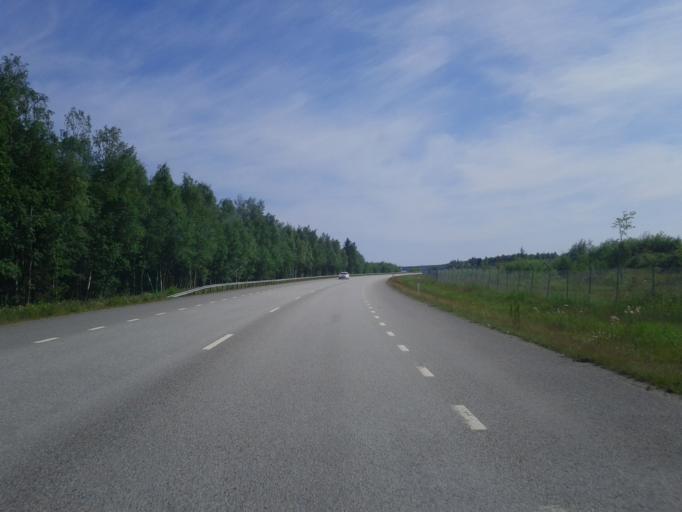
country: SE
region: Vaesterbotten
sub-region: Umea Kommun
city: Umea
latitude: 63.7859
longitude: 20.3031
